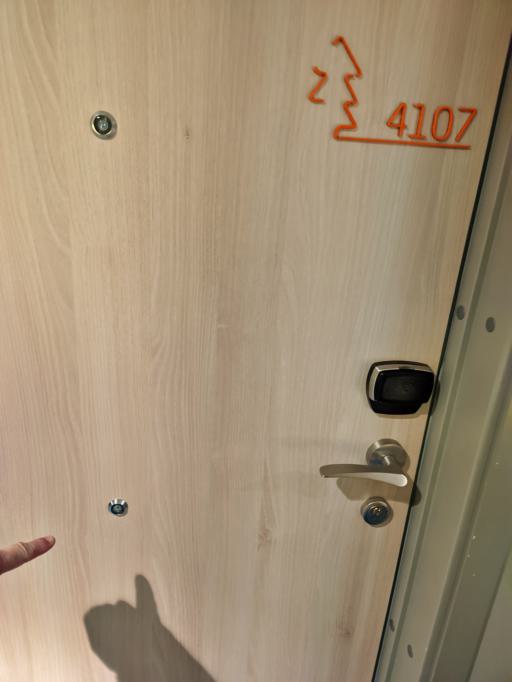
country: NO
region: Akershus
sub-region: Ullensaker
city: Jessheim
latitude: 60.1635
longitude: 11.1622
